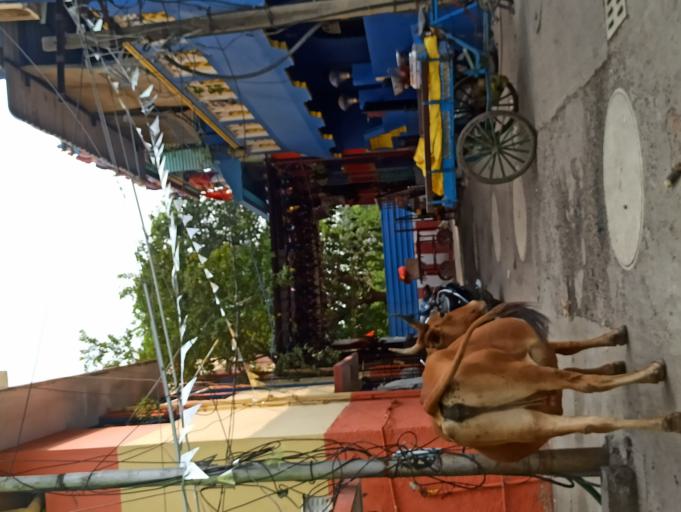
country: IN
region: Tamil Nadu
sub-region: Chennai
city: Chetput
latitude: 13.0607
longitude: 80.2067
